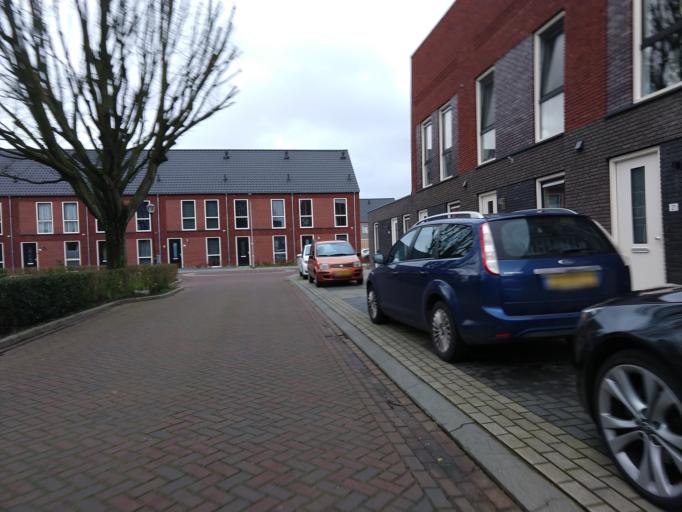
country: NL
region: Zeeland
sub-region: Gemeente Goes
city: Goes
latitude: 51.5012
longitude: 3.8802
